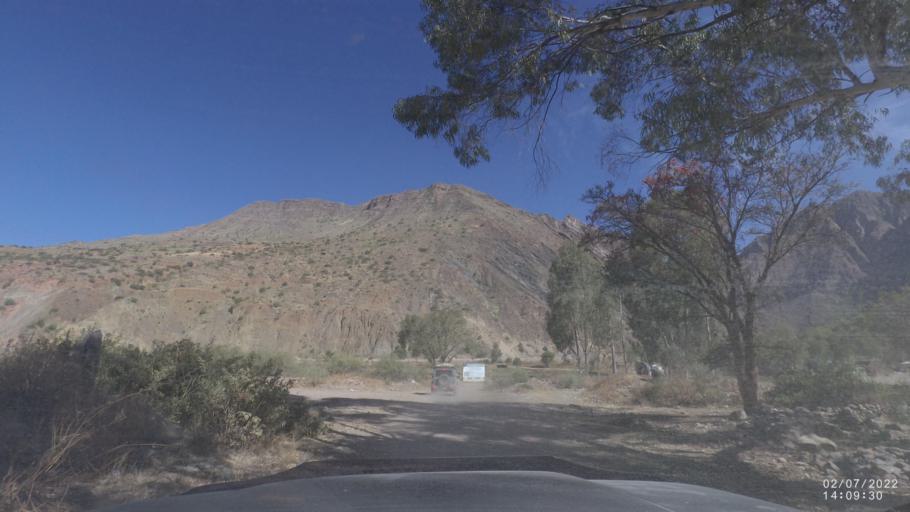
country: BO
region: Cochabamba
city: Irpa Irpa
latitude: -17.8223
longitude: -66.4020
